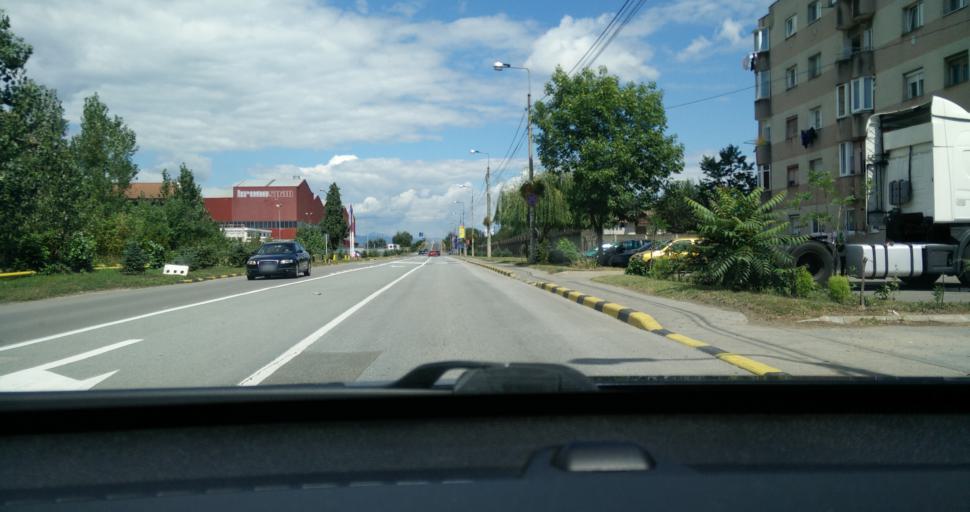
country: RO
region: Alba
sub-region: Municipiul Sebes
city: Sebes
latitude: 45.9675
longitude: 23.5576
